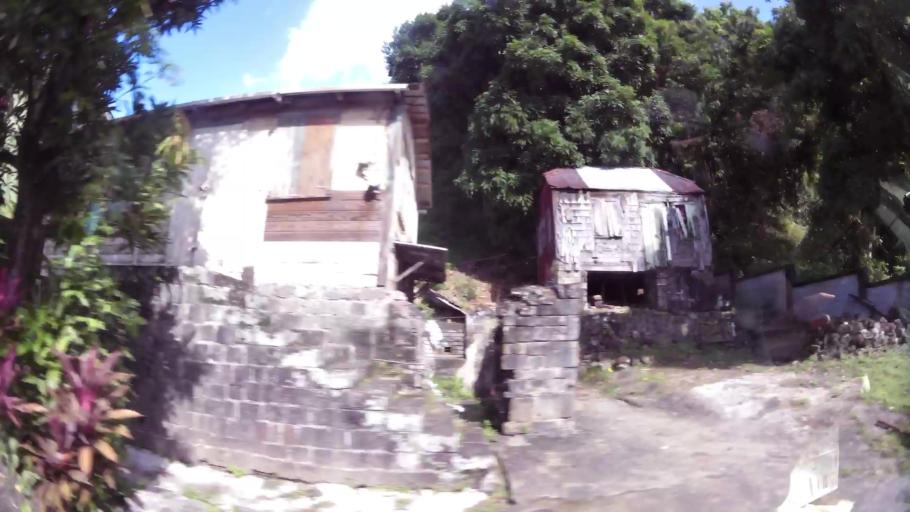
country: DM
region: Saint George
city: Roseau
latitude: 15.2903
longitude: -61.3774
